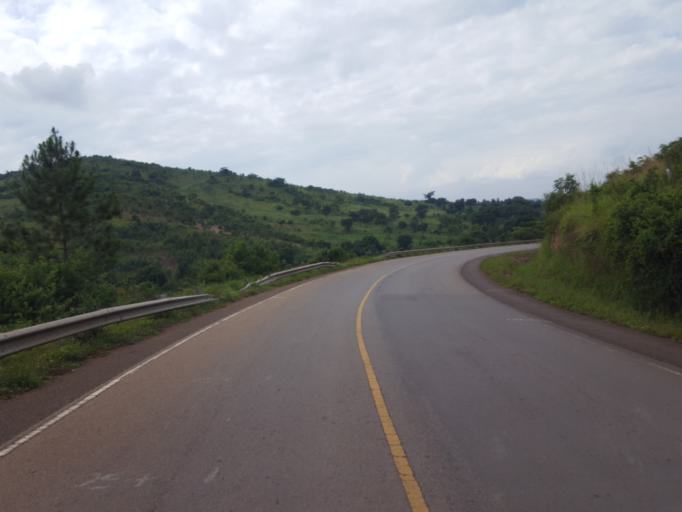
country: UG
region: Central Region
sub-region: Mityana District
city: Mityana
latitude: 0.6248
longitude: 32.1335
